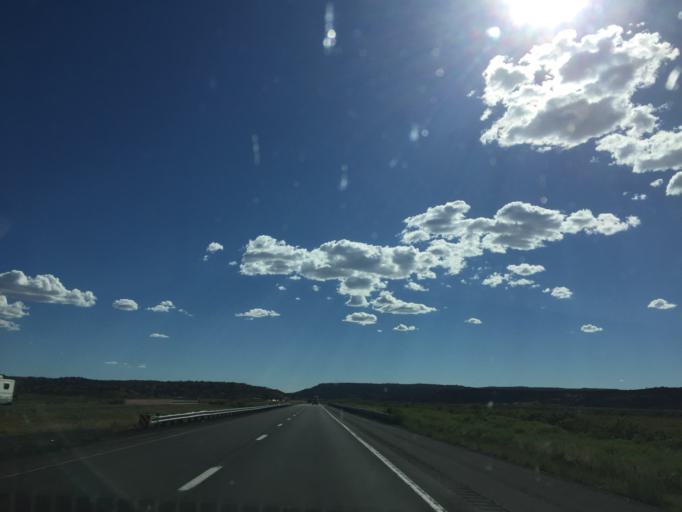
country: US
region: New Mexico
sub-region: McKinley County
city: Gallup
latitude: 35.4820
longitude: -108.9110
